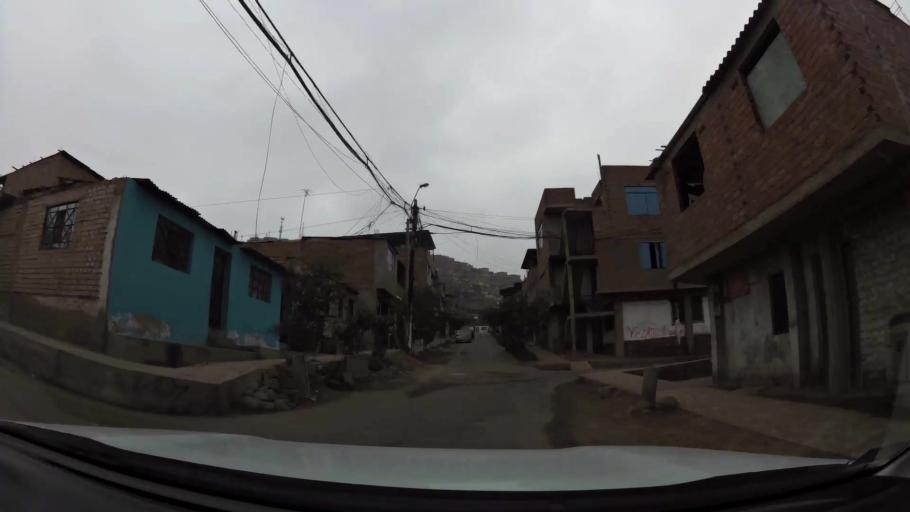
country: PE
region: Lima
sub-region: Lima
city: Surco
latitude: -12.1777
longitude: -76.9499
